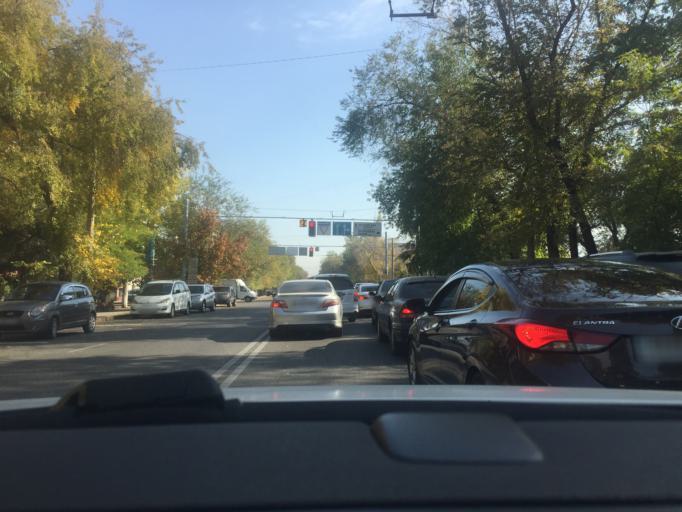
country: KZ
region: Almaty Qalasy
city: Almaty
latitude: 43.2613
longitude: 76.9346
